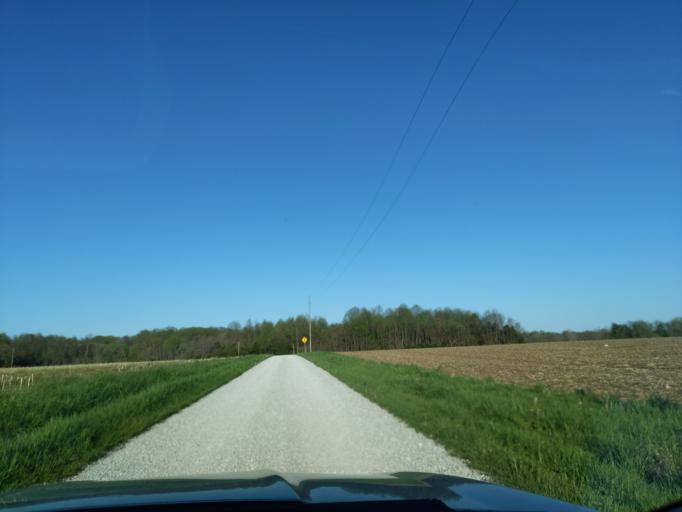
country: US
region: Indiana
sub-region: Decatur County
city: Westport
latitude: 39.1969
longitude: -85.4477
